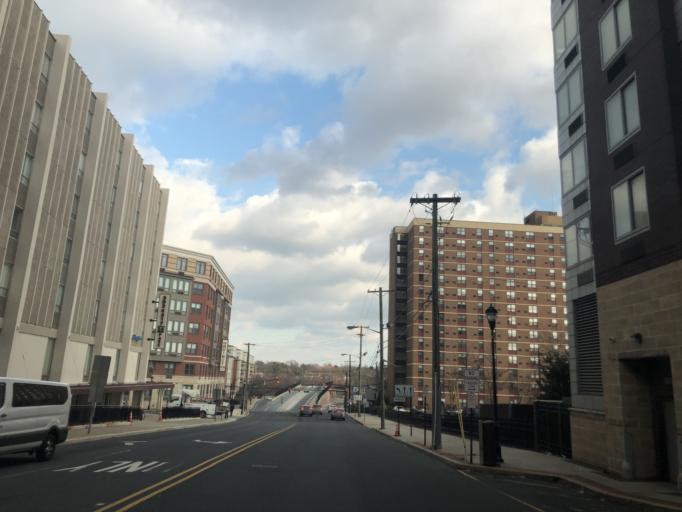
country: US
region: New Jersey
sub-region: Middlesex County
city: New Brunswick
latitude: 40.4923
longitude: -74.4431
